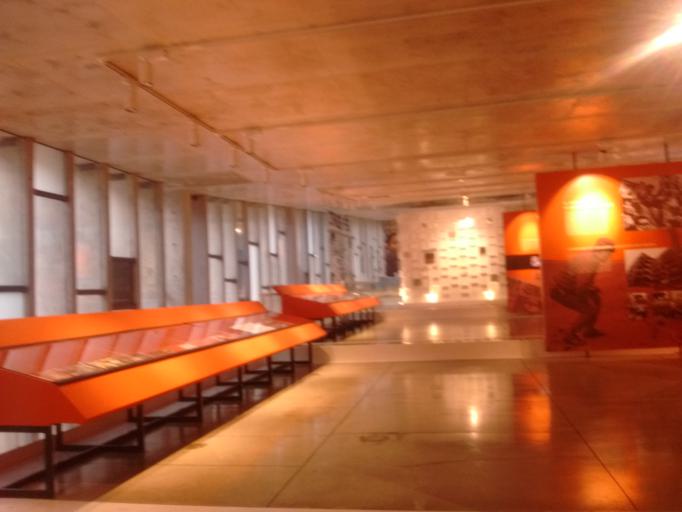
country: PE
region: Lima
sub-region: Lima
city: San Isidro
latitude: -12.1100
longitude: -77.0537
